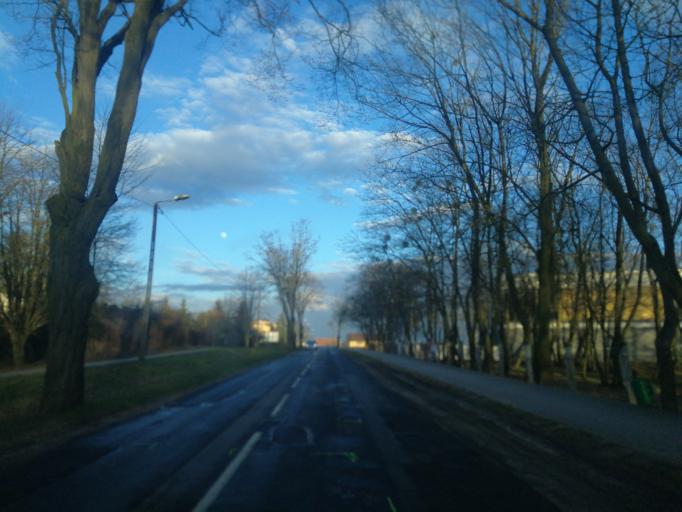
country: PL
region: Kujawsko-Pomorskie
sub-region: Powiat torunski
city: Chelmza
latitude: 53.1884
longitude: 18.6260
